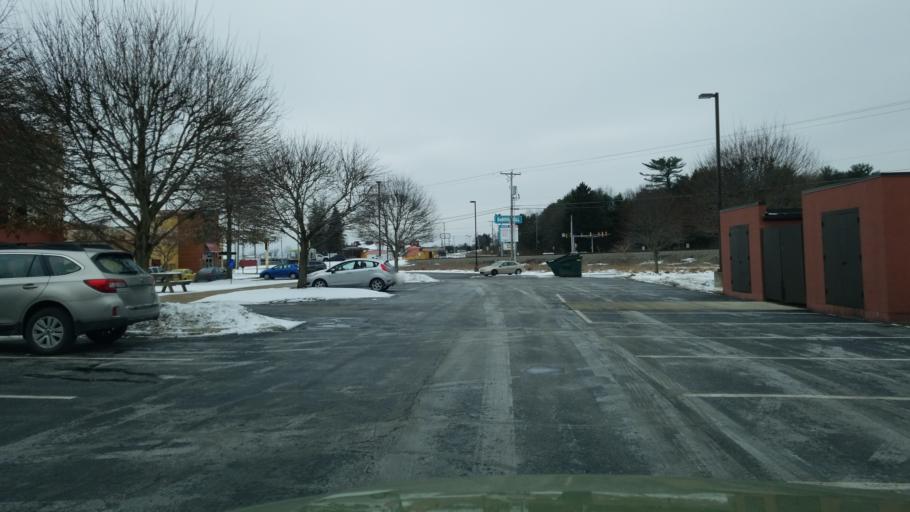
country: US
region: Pennsylvania
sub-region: Clearfield County
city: DuBois
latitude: 41.1220
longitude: -78.7226
